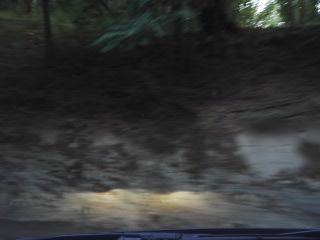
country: IT
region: Calabria
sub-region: Provincia di Vibo-Valentia
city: Nardodipace
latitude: 38.4452
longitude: 16.3379
